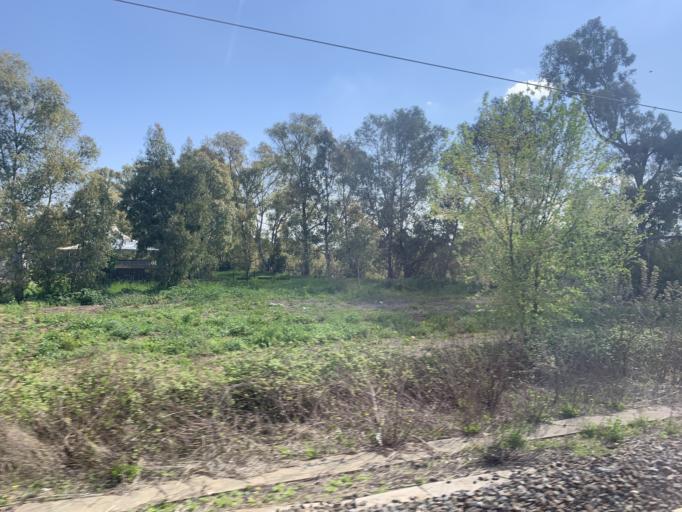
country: IT
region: Latium
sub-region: Citta metropolitana di Roma Capitale
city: Ciampino
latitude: 41.8279
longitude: 12.5709
